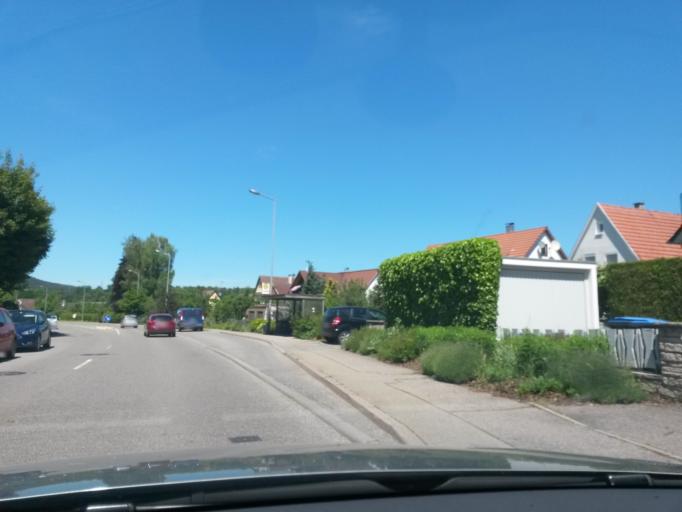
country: DE
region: Baden-Wuerttemberg
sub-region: Regierungsbezirk Stuttgart
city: Weil der Stadt
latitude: 48.7715
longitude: 8.8478
